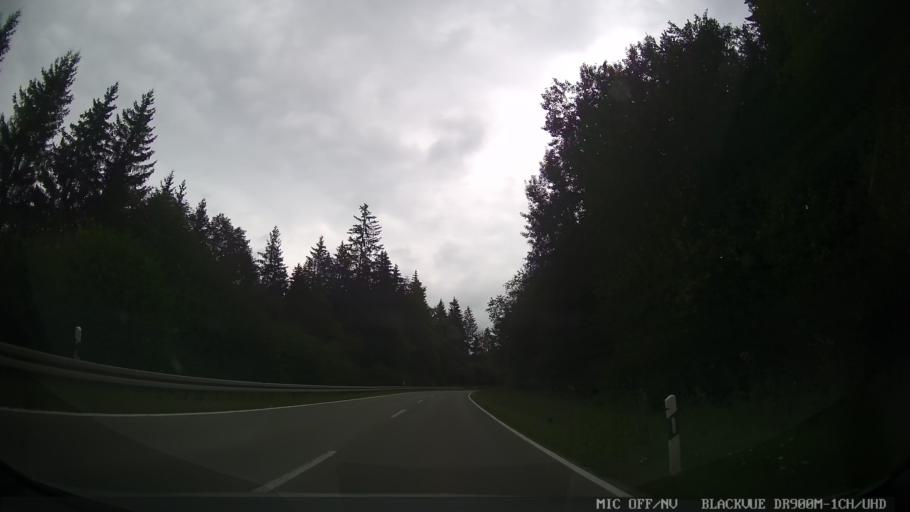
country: DE
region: Baden-Wuerttemberg
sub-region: Freiburg Region
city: Neuhausen ob Eck
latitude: 47.9949
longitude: 8.9313
